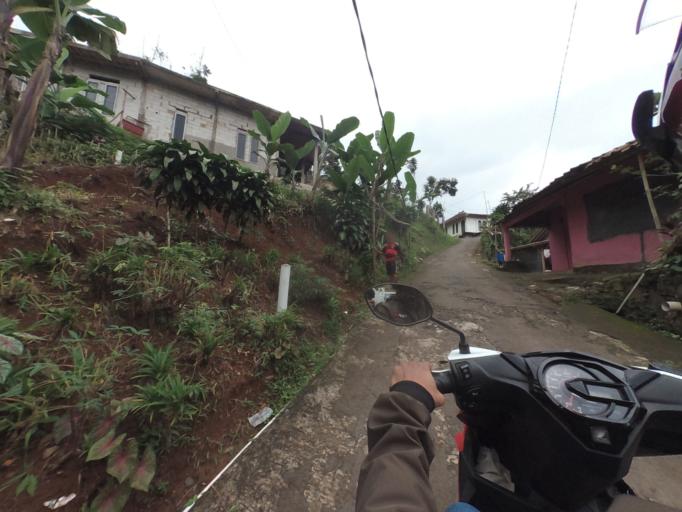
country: ID
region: West Java
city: Bogor
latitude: -6.6146
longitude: 106.7336
